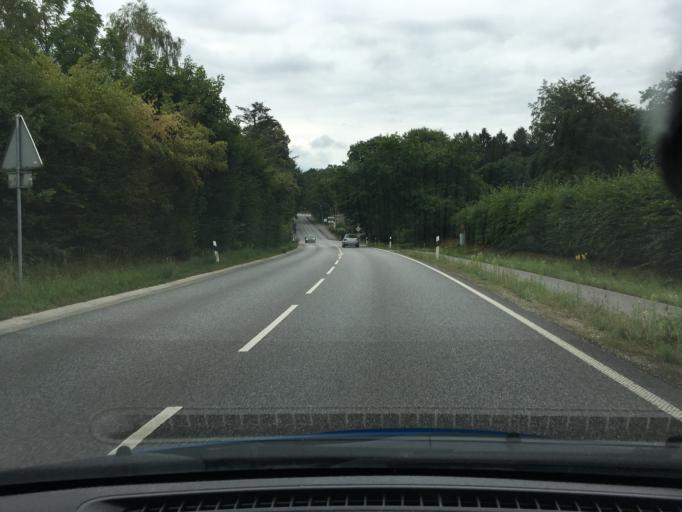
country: DE
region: Schleswig-Holstein
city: Hamwarde
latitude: 53.4248
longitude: 10.4129
